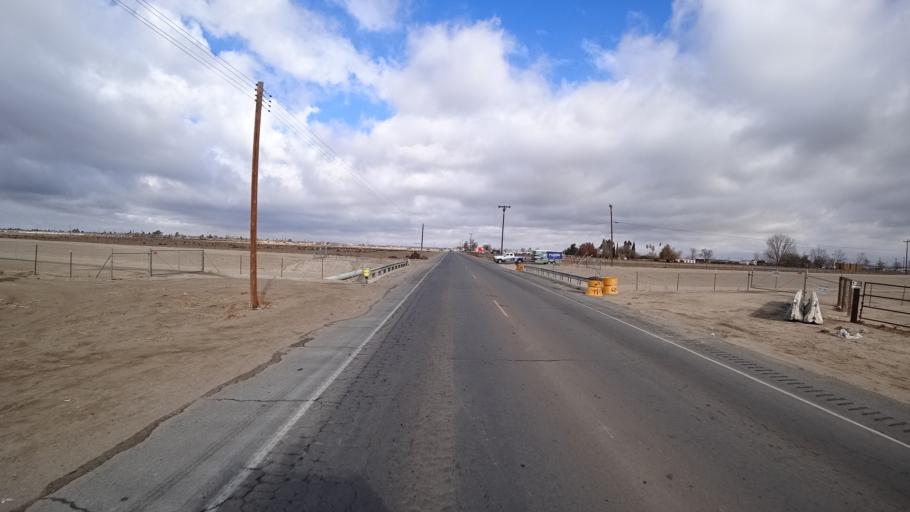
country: US
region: California
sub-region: Kern County
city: Greenfield
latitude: 35.2915
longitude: -118.9855
